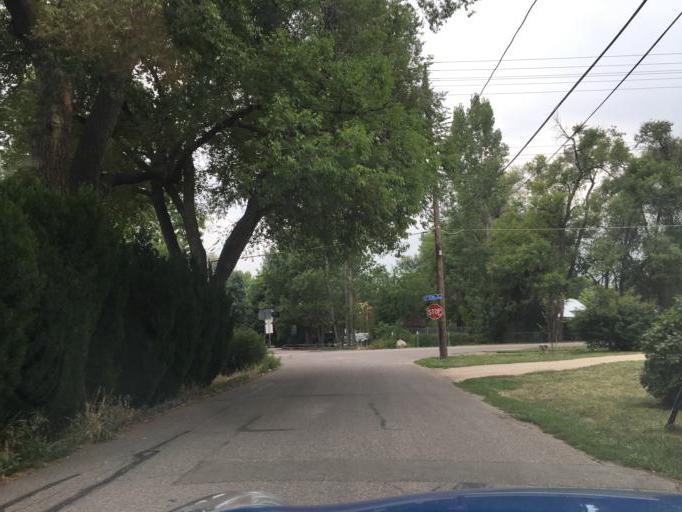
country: US
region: Colorado
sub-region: Jefferson County
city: Wheat Ridge
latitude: 39.7479
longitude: -105.1000
